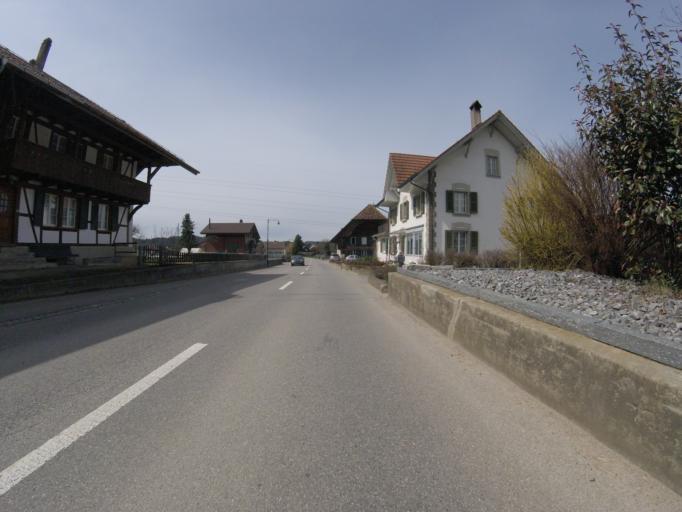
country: CH
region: Bern
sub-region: Bern-Mittelland District
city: Laupen
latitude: 46.9108
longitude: 7.2256
